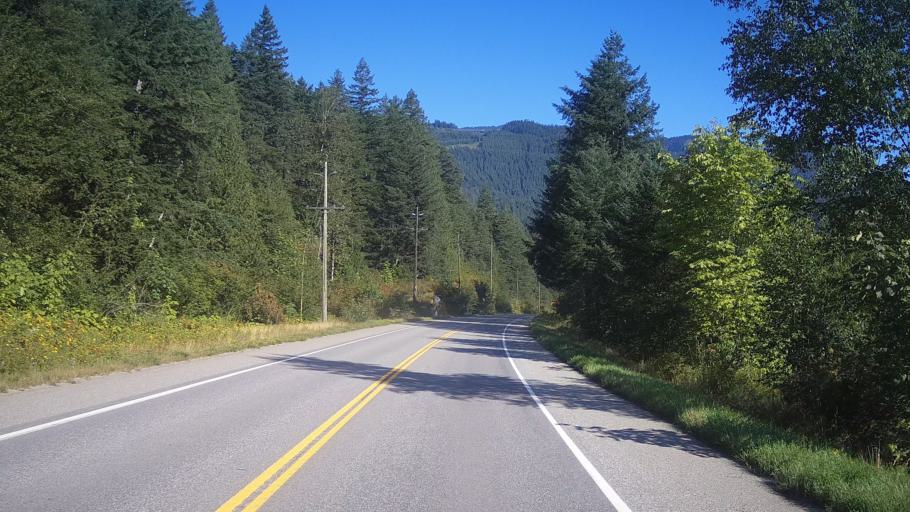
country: CA
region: British Columbia
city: Hope
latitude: 49.5407
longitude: -121.4359
